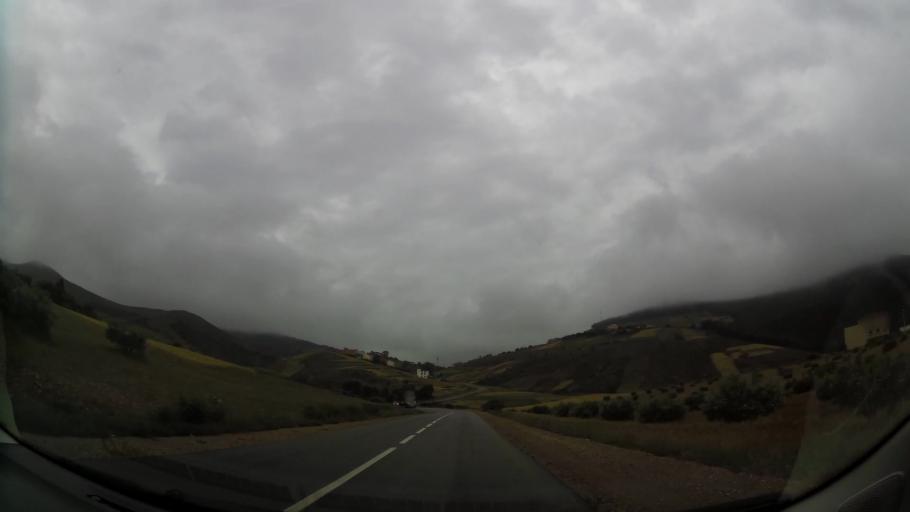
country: MA
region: Oriental
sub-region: Nador
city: Nador
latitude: 35.1375
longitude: -3.0522
